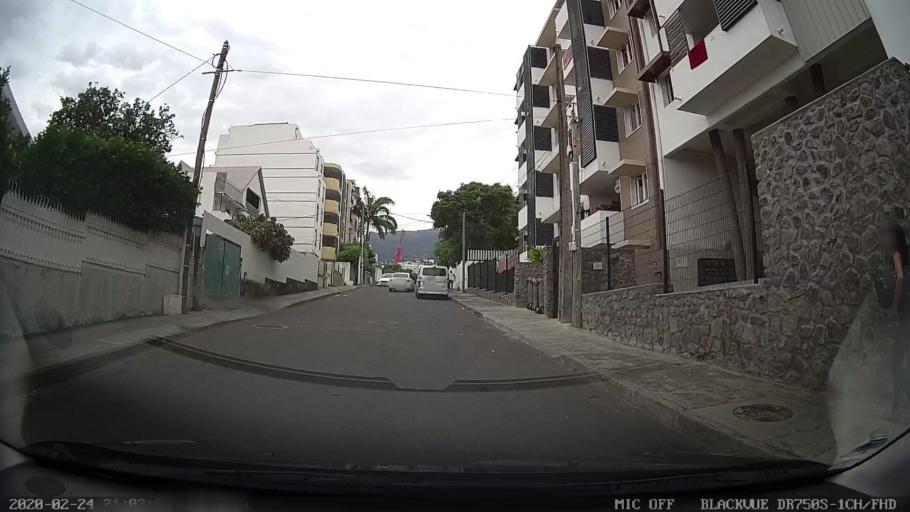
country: RE
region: Reunion
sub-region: Reunion
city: Saint-Denis
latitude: -20.8954
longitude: 55.4839
